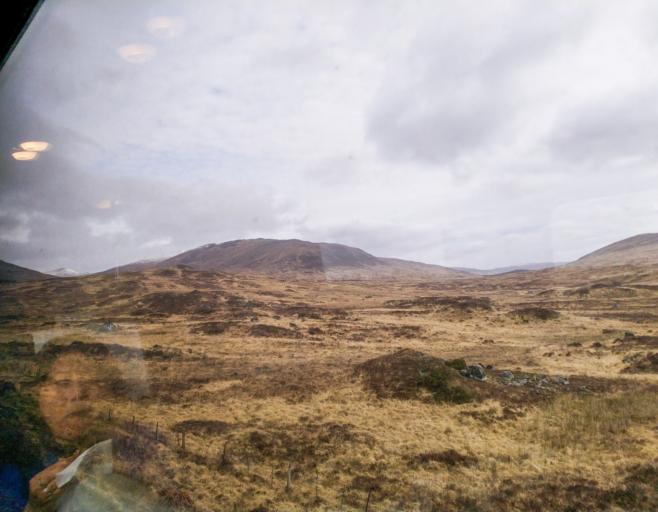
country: GB
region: Scotland
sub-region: Highland
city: Spean Bridge
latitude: 56.6979
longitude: -4.5758
